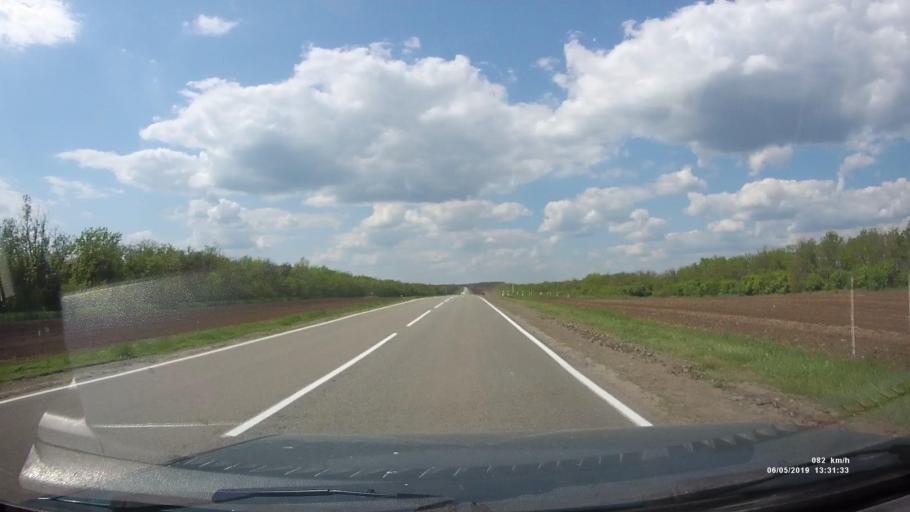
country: RU
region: Rostov
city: Ust'-Donetskiy
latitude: 47.6775
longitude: 40.8089
